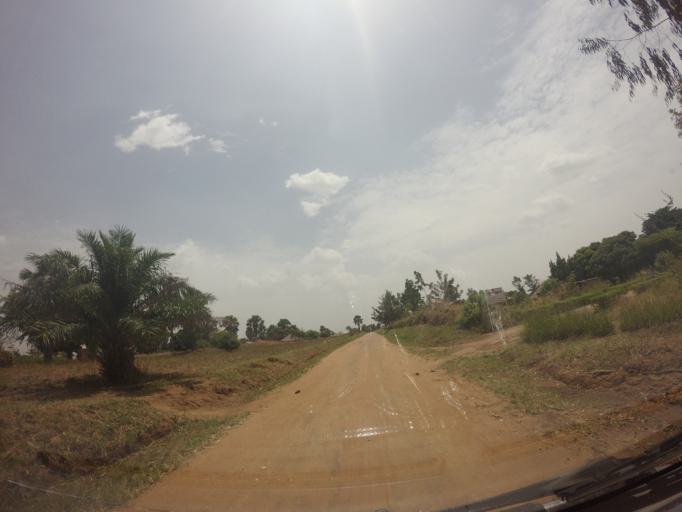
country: UG
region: Northern Region
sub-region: Arua District
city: Arua
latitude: 2.9511
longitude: 30.9140
